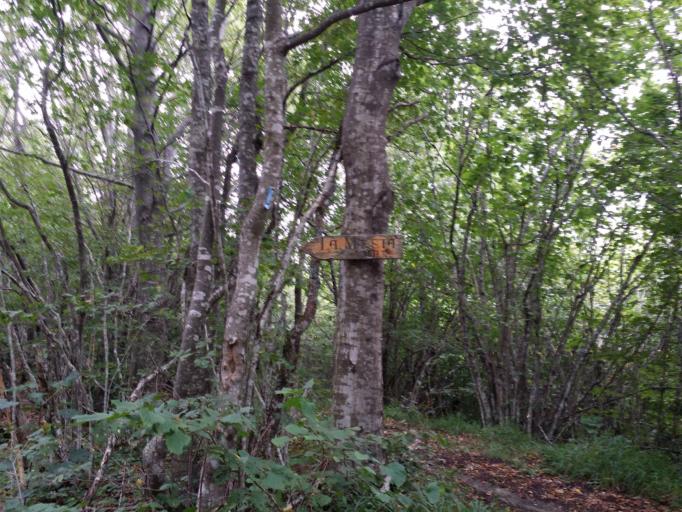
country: IT
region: Emilia-Romagna
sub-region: Provincia di Parma
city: Borgo Val di Taro
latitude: 44.5495
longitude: 9.7901
